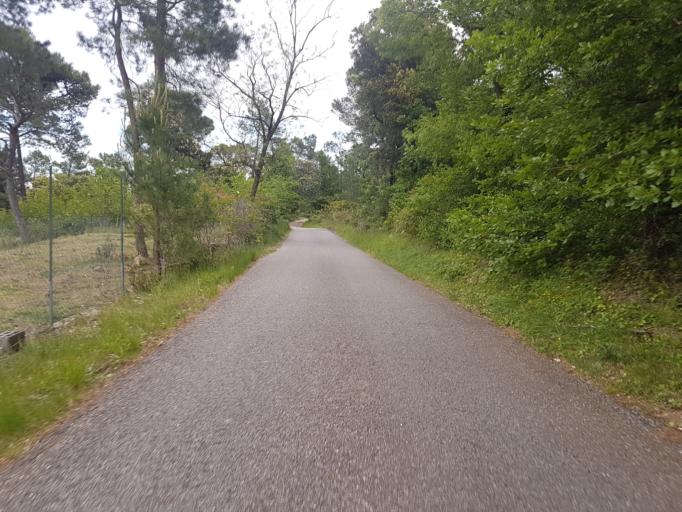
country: FR
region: Provence-Alpes-Cote d'Azur
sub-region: Departement du Vaucluse
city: Mondragon
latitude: 44.2415
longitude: 4.7235
